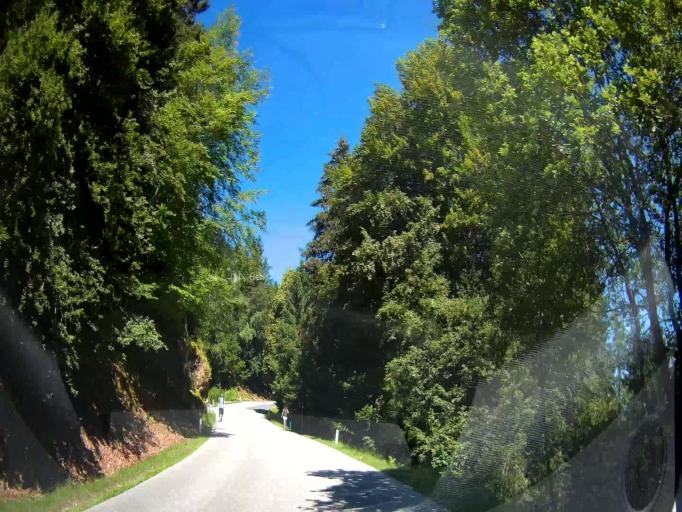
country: AT
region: Carinthia
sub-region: Politischer Bezirk Klagenfurt Land
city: Maria Worth
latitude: 46.6091
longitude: 14.1486
